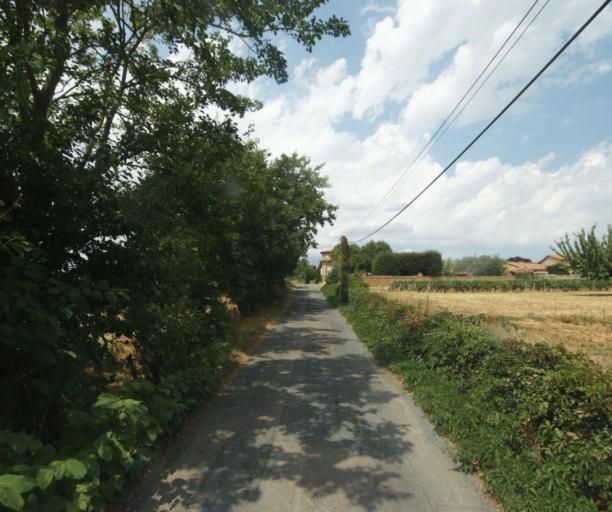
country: FR
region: Rhone-Alpes
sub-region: Departement du Rhone
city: Saint-Germain-Nuelles
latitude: 45.8604
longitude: 4.5995
